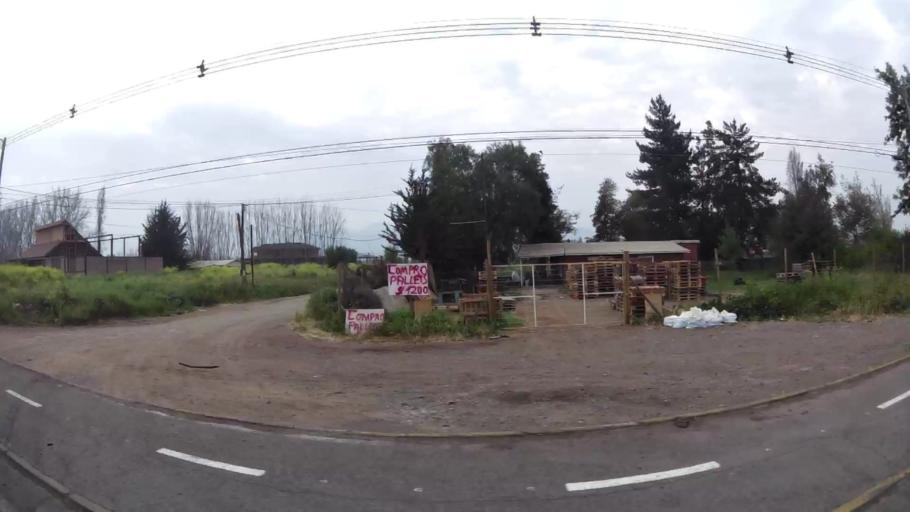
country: CL
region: Santiago Metropolitan
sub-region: Provincia de Chacabuco
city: Lampa
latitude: -33.2289
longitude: -70.7728
